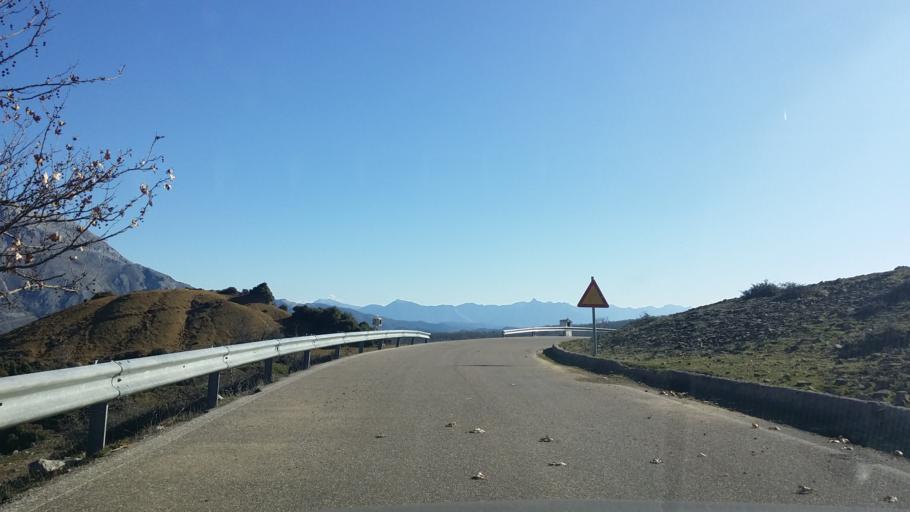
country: GR
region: West Greece
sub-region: Nomos Aitolias kai Akarnanias
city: Krikellos
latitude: 39.0128
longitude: 21.2715
